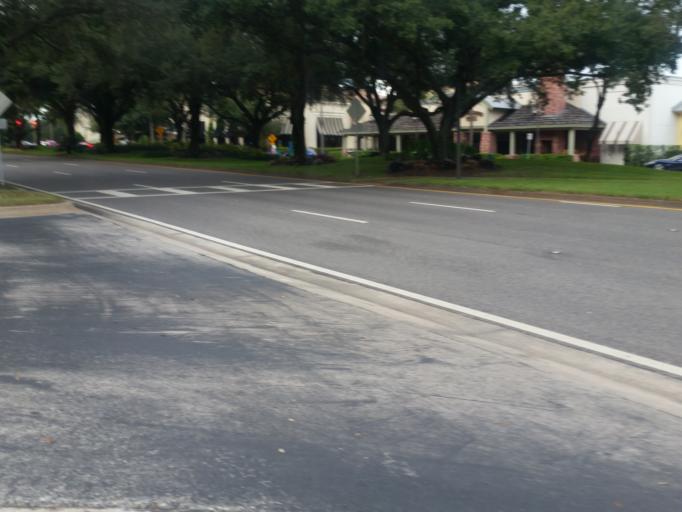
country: US
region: Florida
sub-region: Orange County
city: Doctor Phillips
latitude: 28.4318
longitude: -81.4712
